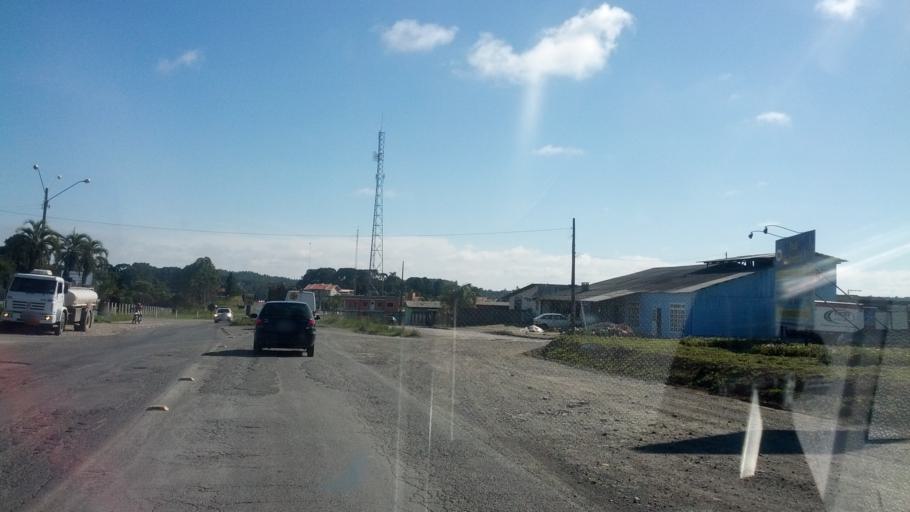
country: BR
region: Santa Catarina
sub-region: Otacilio Costa
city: Otacilio Costa
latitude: -27.5818
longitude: -50.1625
